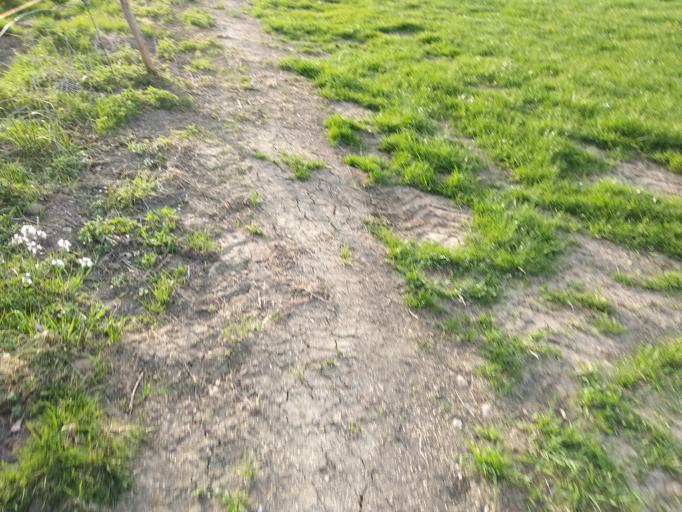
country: DE
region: Bavaria
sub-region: Swabia
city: Lautrach
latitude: 47.8951
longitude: 10.1378
